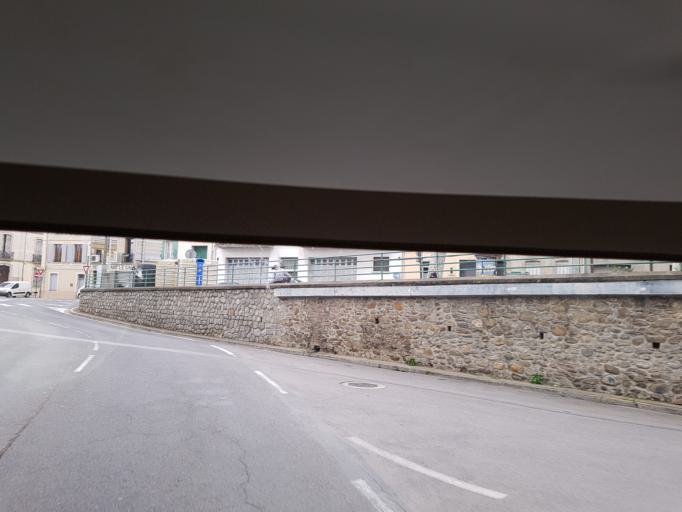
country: FR
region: Languedoc-Roussillon
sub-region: Departement des Pyrenees-Orientales
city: Prades
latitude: 42.6185
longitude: 2.4282
